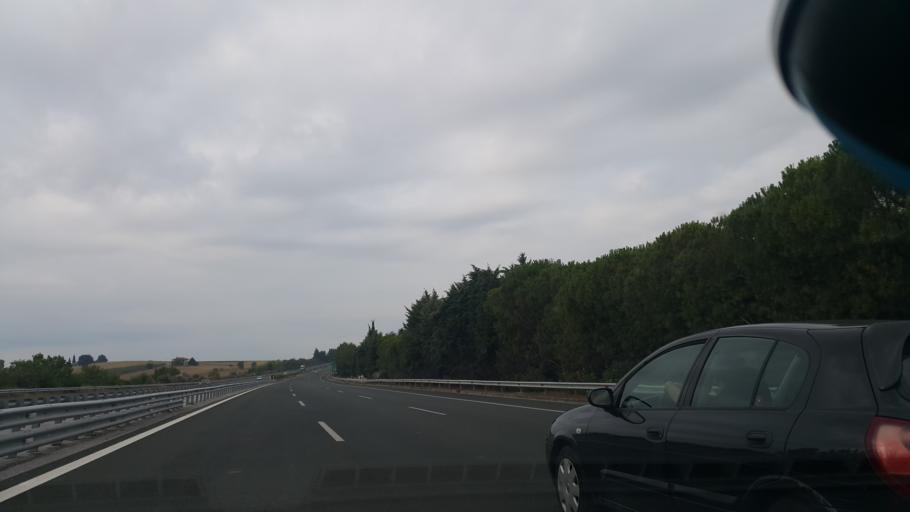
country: GR
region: Central Macedonia
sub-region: Nomos Pierias
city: Kitros
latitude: 40.3764
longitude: 22.6067
